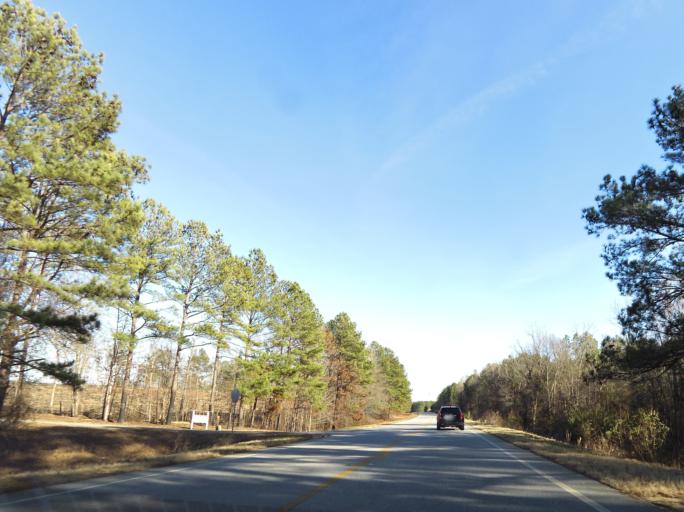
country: US
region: Georgia
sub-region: Crawford County
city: Roberta
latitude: 32.7236
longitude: -84.0383
